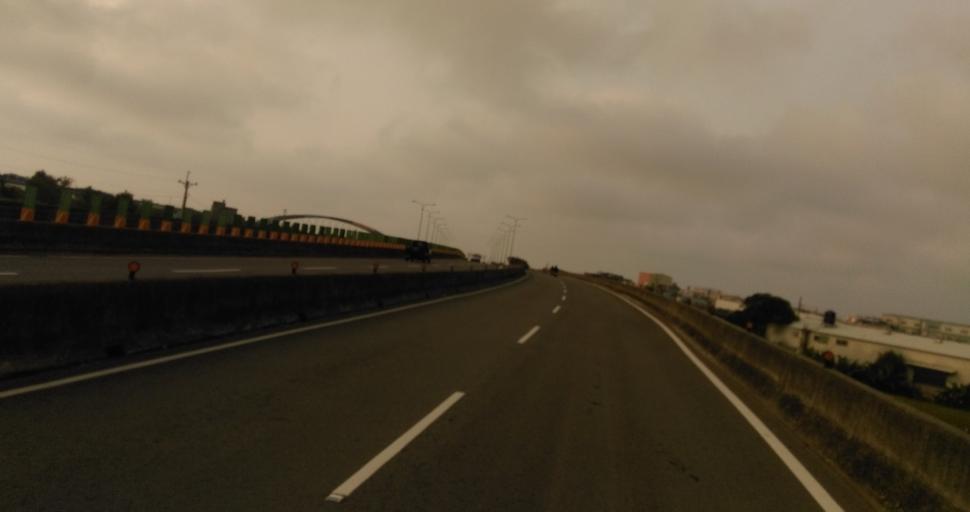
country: TW
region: Taiwan
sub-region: Hsinchu
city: Hsinchu
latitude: 24.8029
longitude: 120.9205
